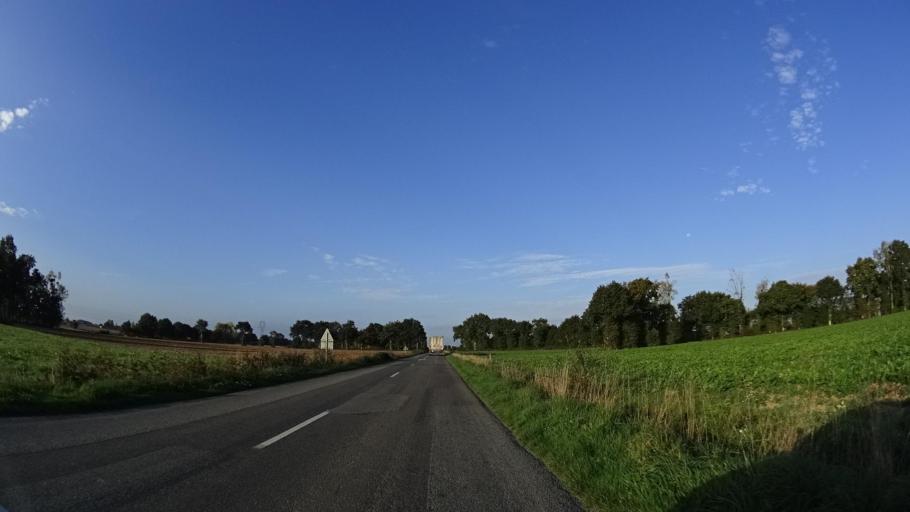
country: FR
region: Brittany
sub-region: Departement d'Ille-et-Vilaine
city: Medreac
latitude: 48.2592
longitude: -2.1007
